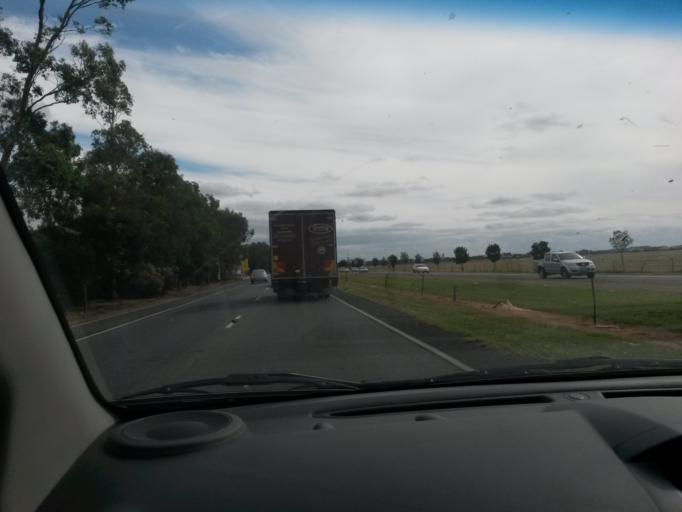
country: AU
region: South Australia
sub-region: Salisbury
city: Salisbury
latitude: -34.7991
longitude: 138.6405
